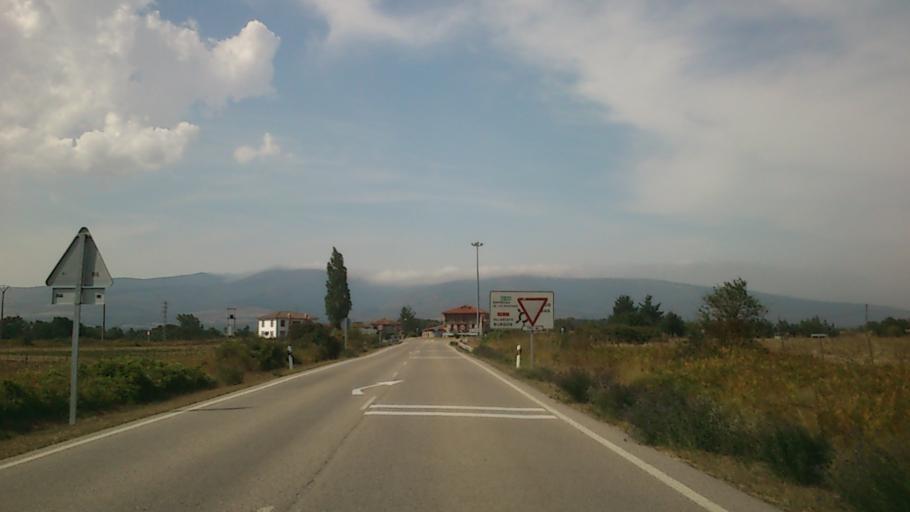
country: ES
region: Castille and Leon
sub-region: Provincia de Burgos
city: Espinosa de los Monteros
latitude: 43.0460
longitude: -3.4856
